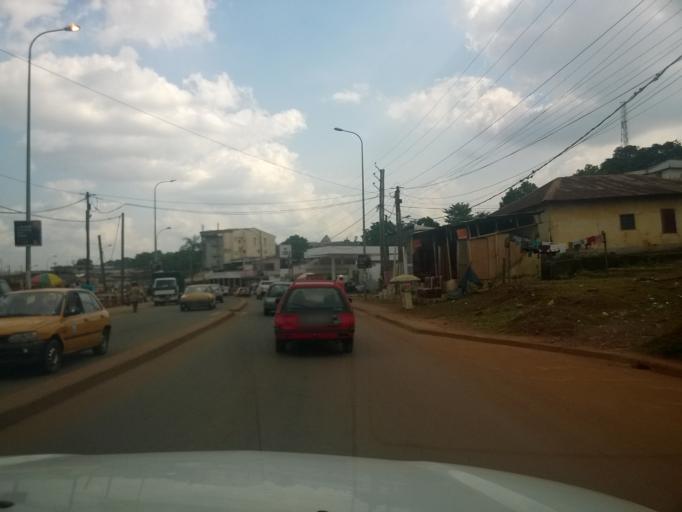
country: CM
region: Centre
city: Yaounde
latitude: 3.8503
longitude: 11.5154
